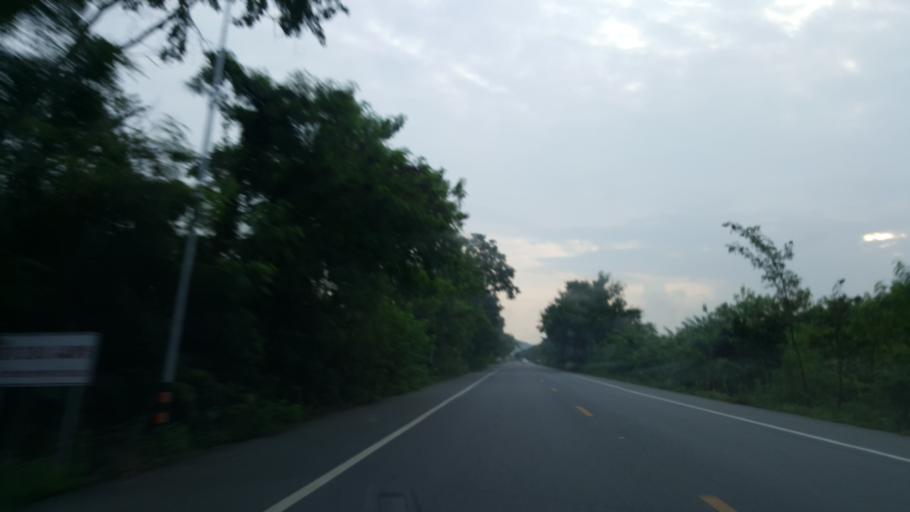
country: TH
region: Chon Buri
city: Sattahip
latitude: 12.7342
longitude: 100.9449
